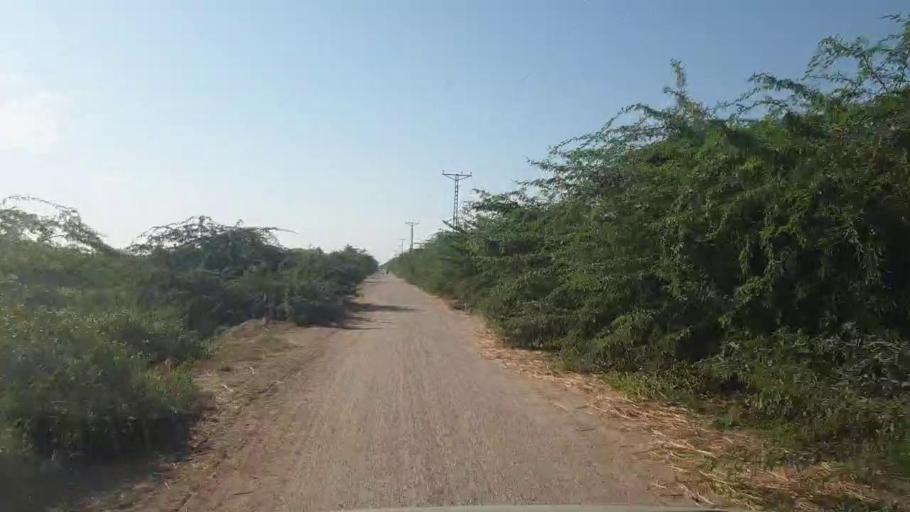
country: PK
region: Sindh
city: Rajo Khanani
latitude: 24.9511
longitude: 68.7944
